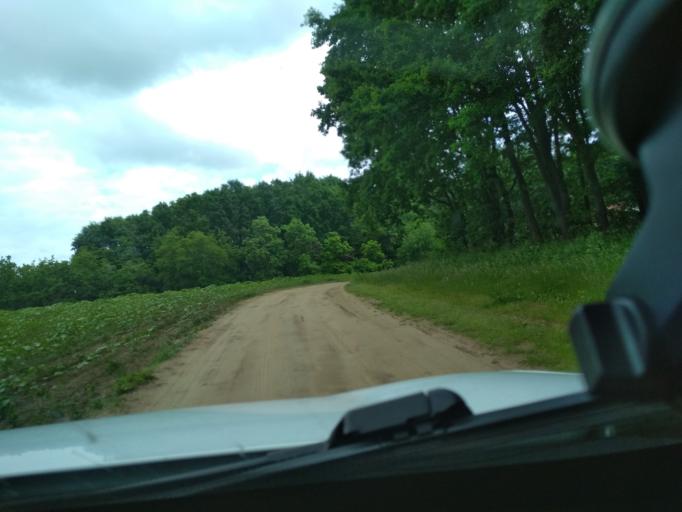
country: HU
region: Jasz-Nagykun-Szolnok
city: Tiszafured
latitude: 47.6197
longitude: 20.7351
